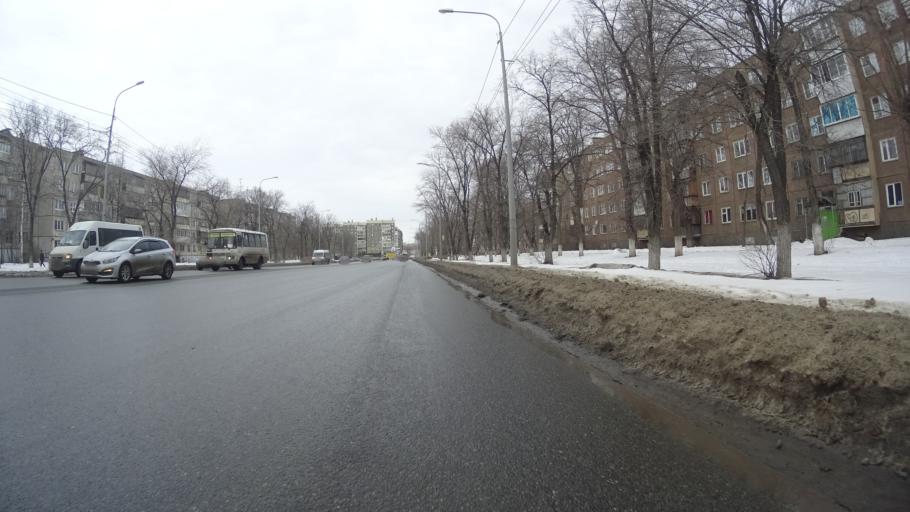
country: RU
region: Chelyabinsk
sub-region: Gorod Chelyabinsk
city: Chelyabinsk
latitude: 55.1959
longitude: 61.3328
